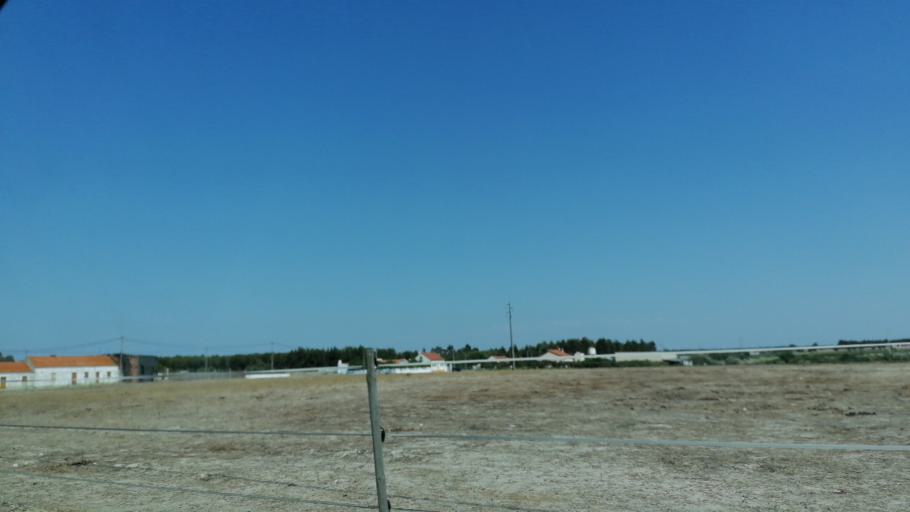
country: PT
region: Santarem
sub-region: Benavente
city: Poceirao
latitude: 38.7088
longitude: -8.7179
